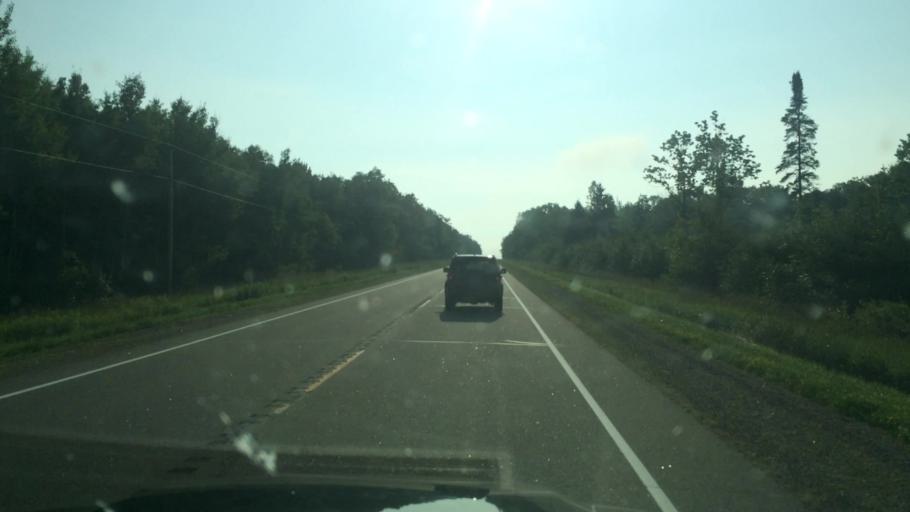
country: US
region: Wisconsin
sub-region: Langlade County
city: Antigo
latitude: 45.1468
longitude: -89.3928
